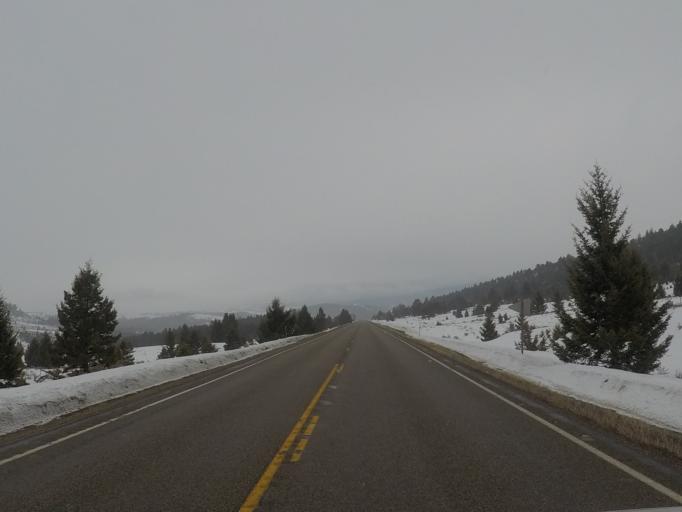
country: US
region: Montana
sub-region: Meagher County
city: White Sulphur Springs
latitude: 46.6426
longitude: -110.8634
